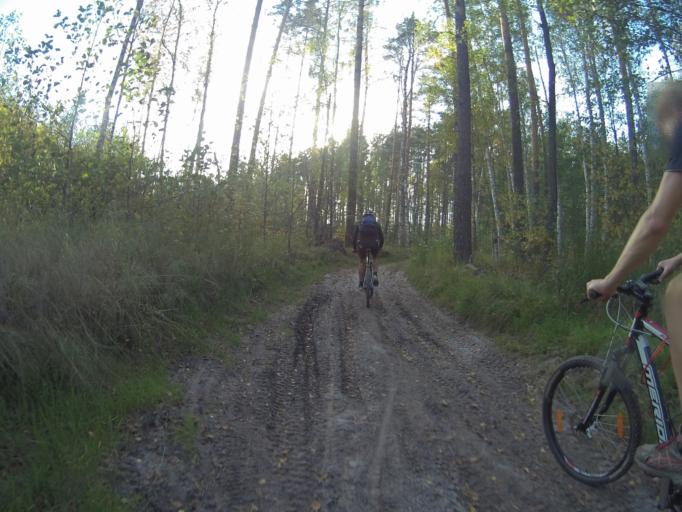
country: RU
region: Vladimir
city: Sobinka
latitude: 55.9519
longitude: 40.0139
